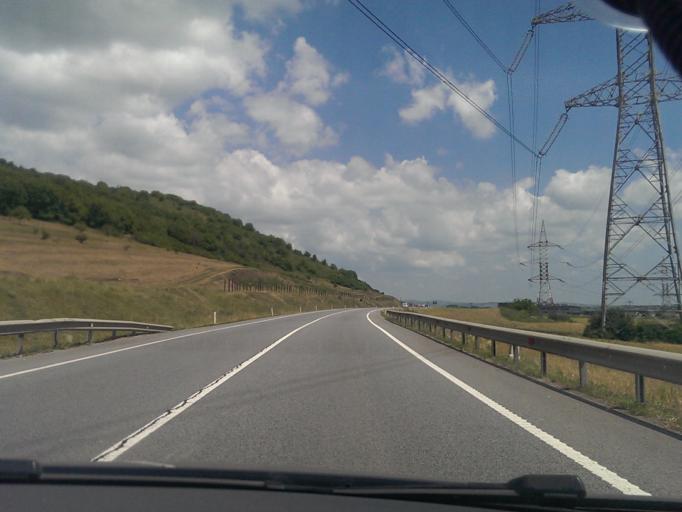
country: RO
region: Cluj
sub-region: Comuna Apahida
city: Apahida
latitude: 46.8147
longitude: 23.7377
